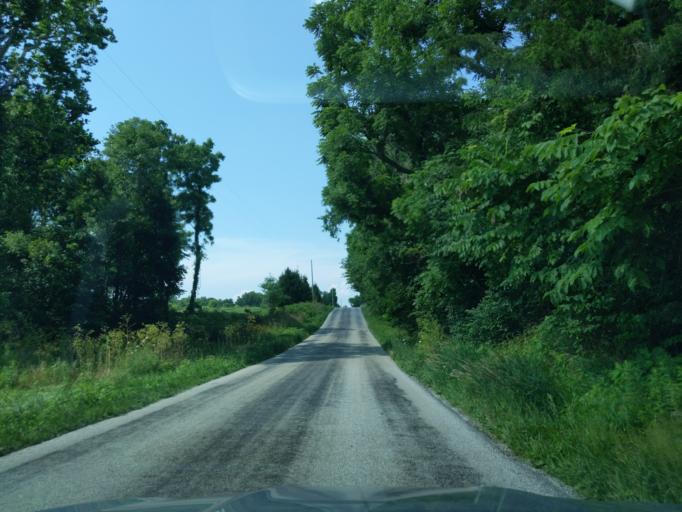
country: US
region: Indiana
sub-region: Ripley County
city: Osgood
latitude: 39.1001
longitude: -85.3452
